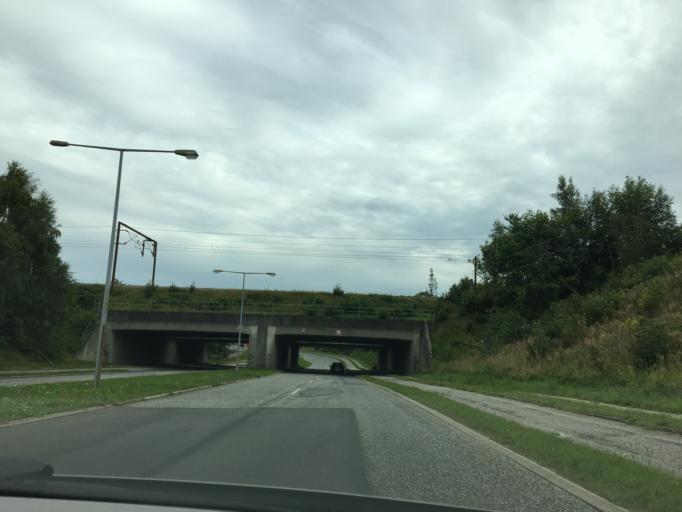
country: DK
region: South Denmark
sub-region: Fredericia Kommune
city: Fredericia
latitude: 55.5590
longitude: 9.7256
